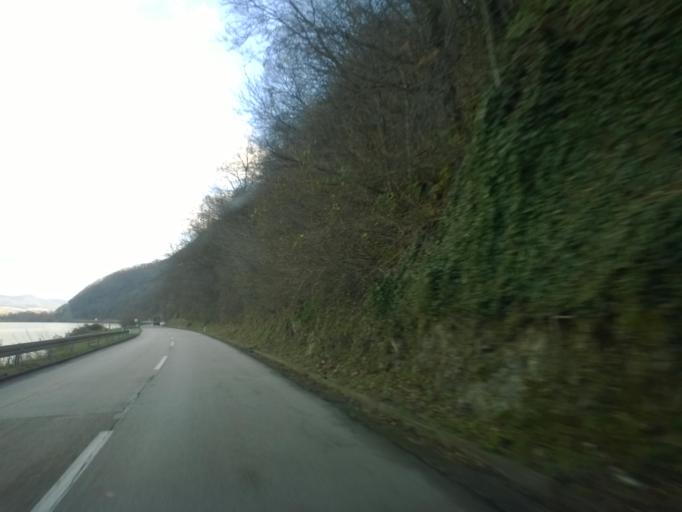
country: RO
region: Caras-Severin
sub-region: Comuna Berzasca
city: Liubcova
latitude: 44.6444
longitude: 21.8211
